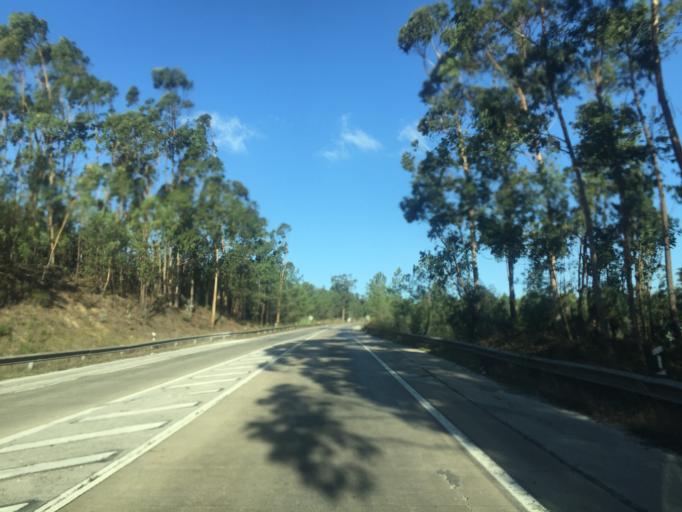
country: PT
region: Santarem
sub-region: Rio Maior
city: Rio Maior
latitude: 39.3261
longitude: -8.9546
